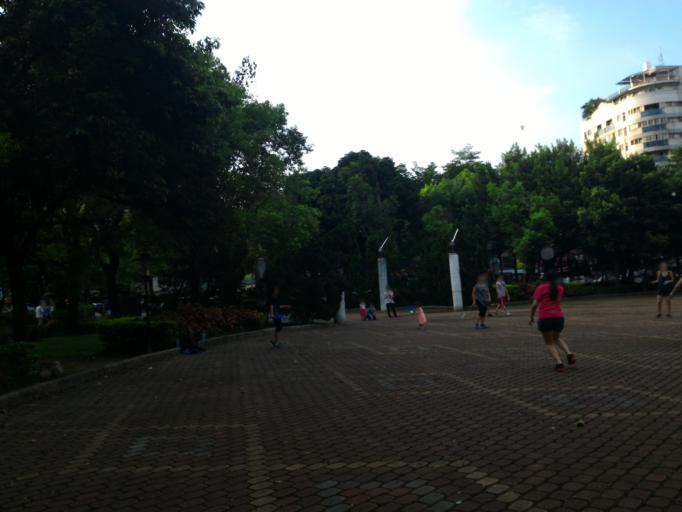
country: TW
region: Taipei
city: Taipei
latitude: 25.0029
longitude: 121.5142
